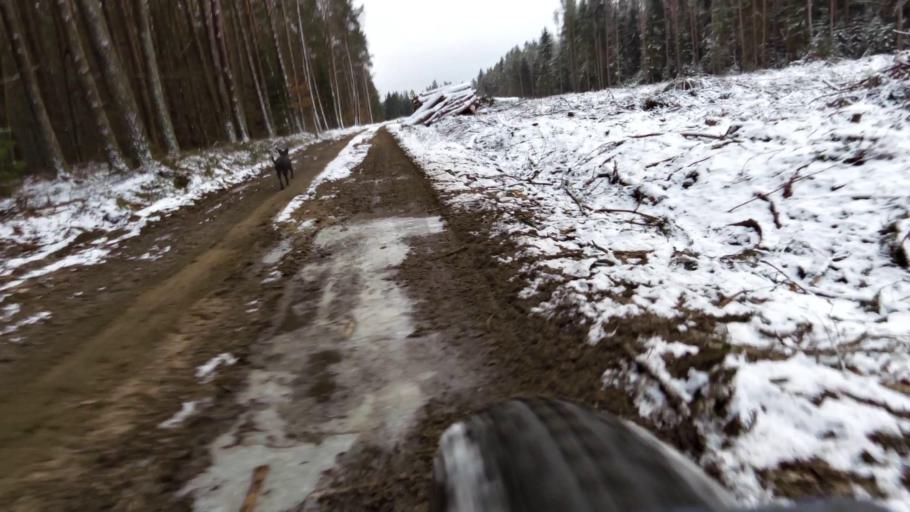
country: PL
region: West Pomeranian Voivodeship
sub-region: Powiat walecki
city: Miroslawiec
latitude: 53.3748
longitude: 16.1481
